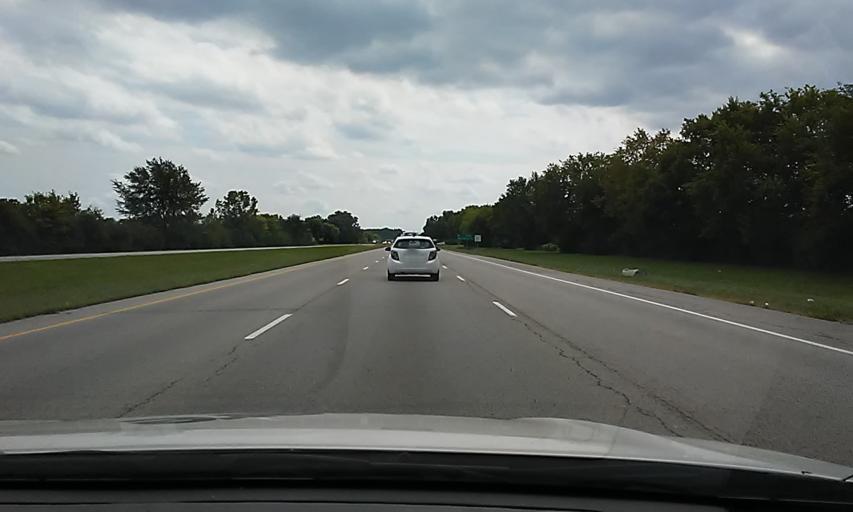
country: US
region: Ohio
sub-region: Clark County
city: Park Layne
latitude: 39.8551
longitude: -84.0576
